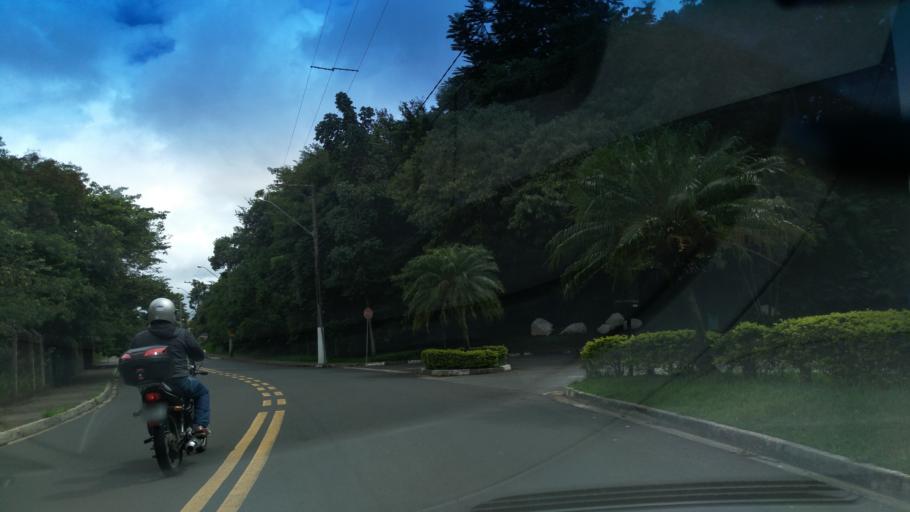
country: BR
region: Sao Paulo
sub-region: Valinhos
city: Valinhos
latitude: -22.9590
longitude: -46.9785
